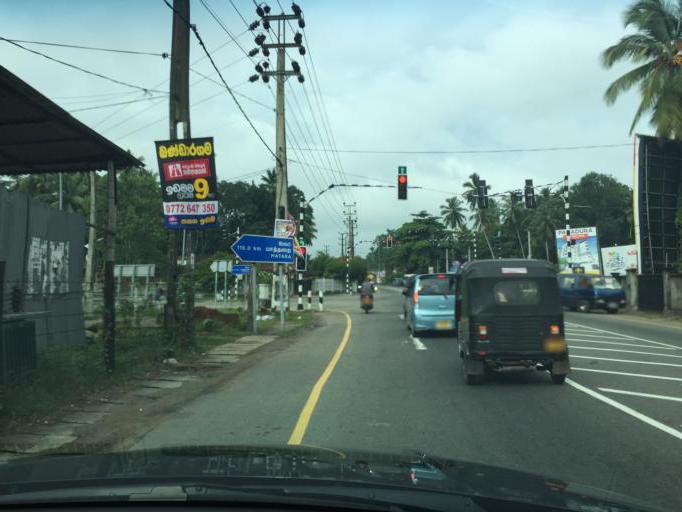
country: LK
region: Western
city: Horana South
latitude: 6.7188
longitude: 80.0035
